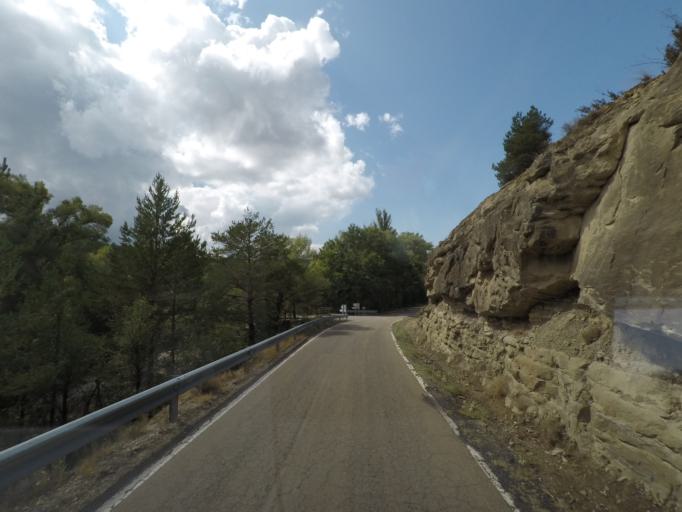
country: ES
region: Aragon
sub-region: Provincia de Huesca
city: Yebra de Basa
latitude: 42.3902
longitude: -0.3114
